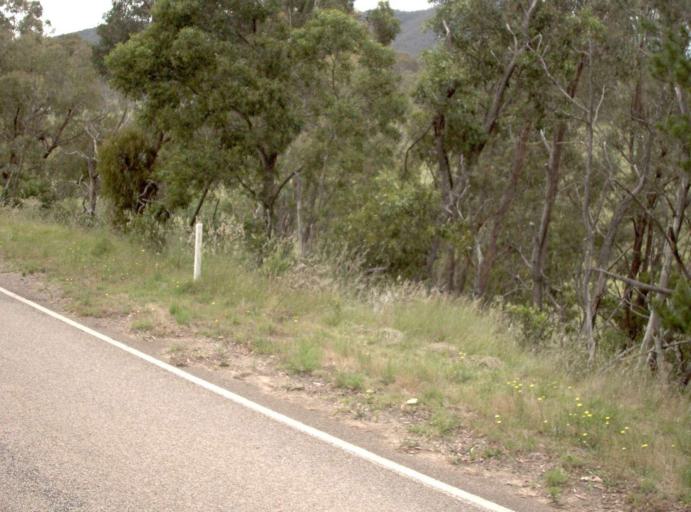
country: AU
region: Victoria
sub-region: East Gippsland
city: Bairnsdale
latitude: -37.5718
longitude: 147.1870
